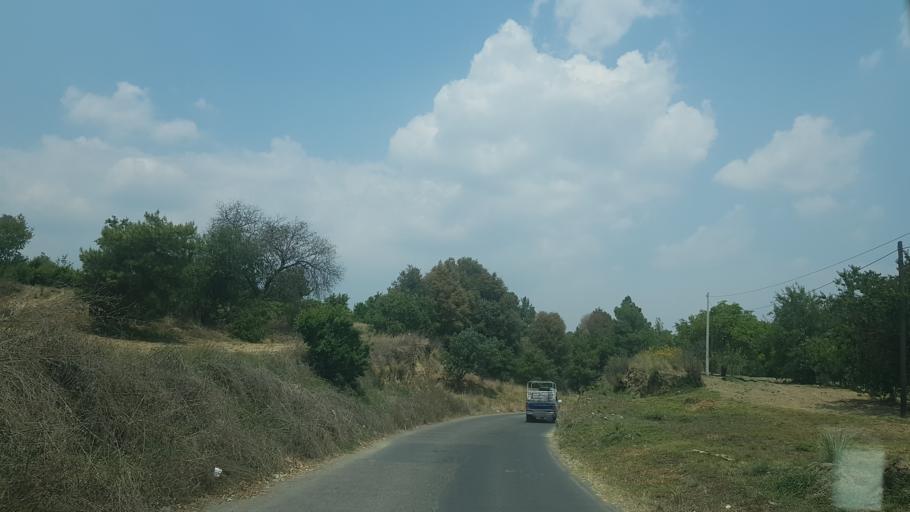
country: MX
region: Puebla
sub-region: San Nicolas de los Ranchos
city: San Pedro Yancuitlalpan
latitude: 19.0907
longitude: -98.4835
